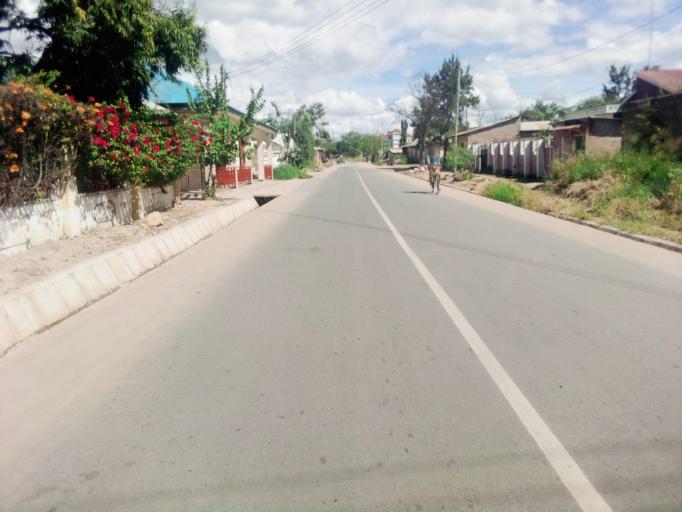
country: TZ
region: Dodoma
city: Dodoma
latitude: -6.1738
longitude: 35.7617
